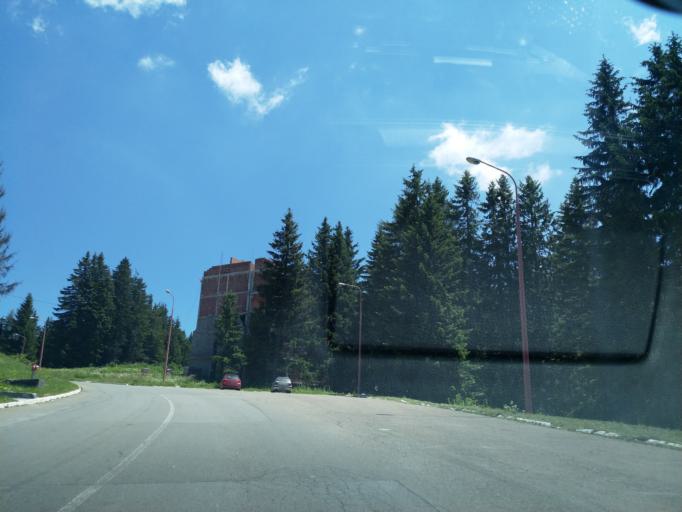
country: RS
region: Central Serbia
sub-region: Raski Okrug
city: Raska
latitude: 43.2866
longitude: 20.7968
